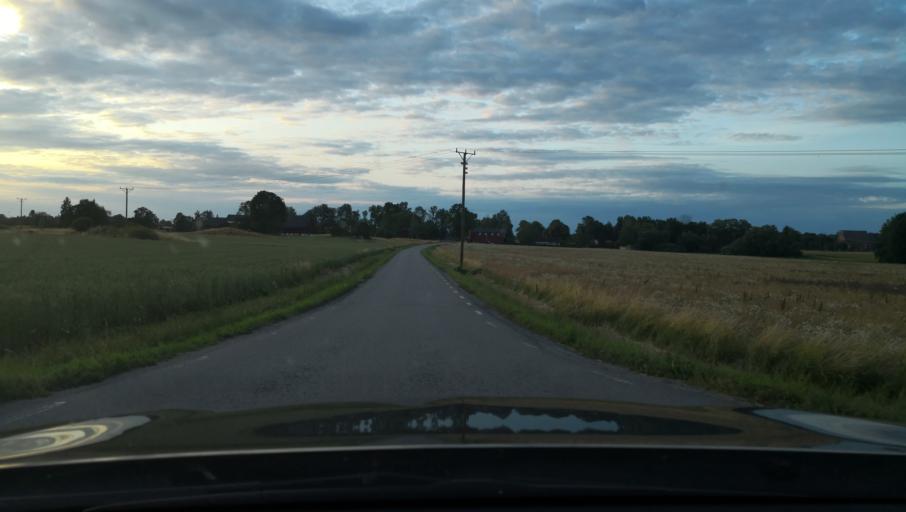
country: SE
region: Uppsala
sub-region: Uppsala Kommun
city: Vattholma
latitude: 60.0338
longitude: 17.6647
